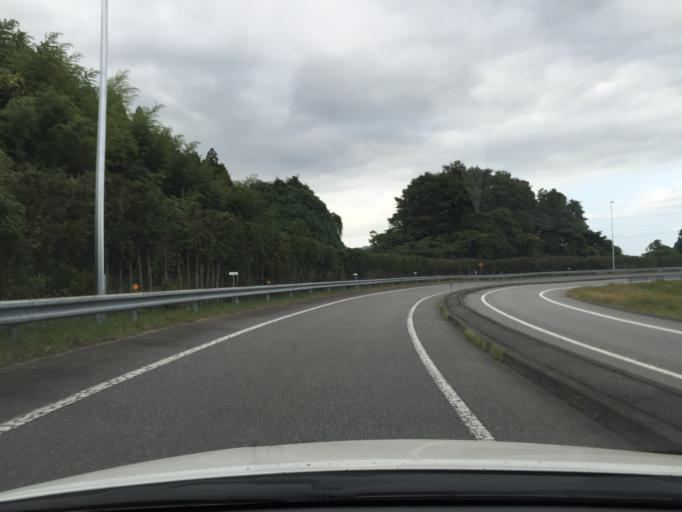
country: JP
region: Ibaraki
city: Kitaibaraki
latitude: 36.9021
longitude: 140.7487
